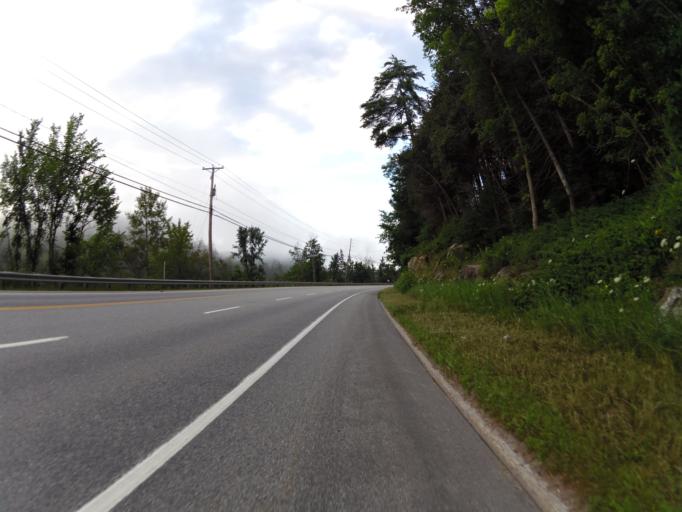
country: CA
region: Quebec
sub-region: Outaouais
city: Wakefield
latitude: 45.6759
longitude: -75.9295
